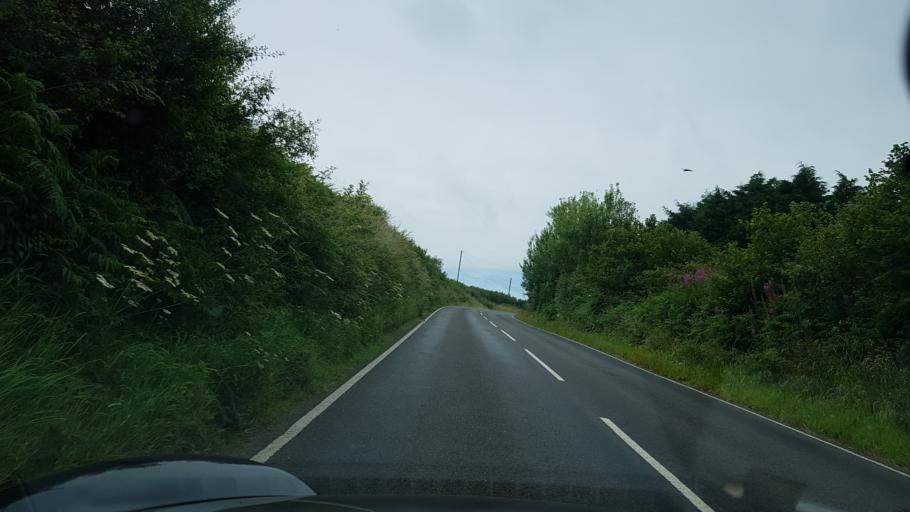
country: GB
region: Wales
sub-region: Pembrokeshire
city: Johnston
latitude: 51.7850
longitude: -5.0239
